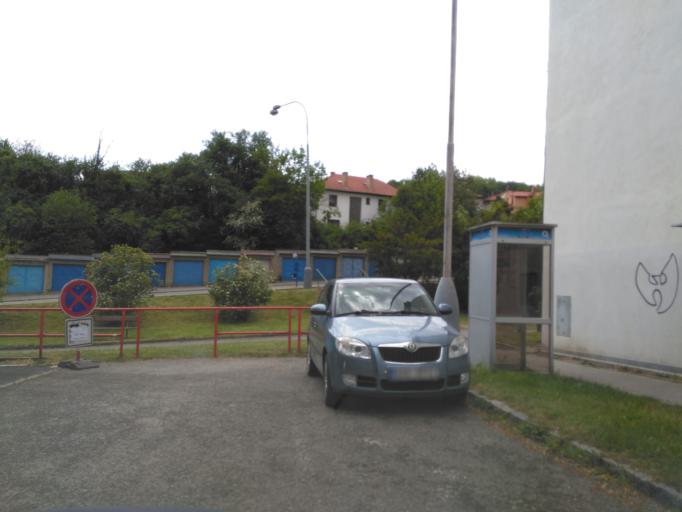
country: CZ
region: Central Bohemia
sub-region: Okres Beroun
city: Beroun
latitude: 49.9659
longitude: 14.0668
